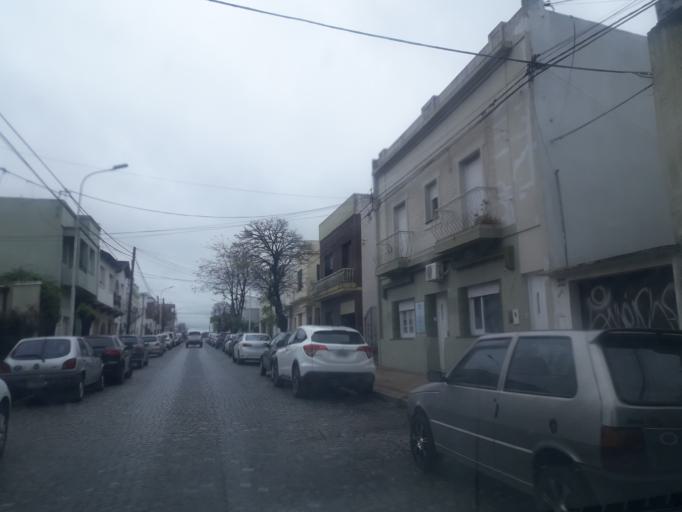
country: AR
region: Buenos Aires
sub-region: Partido de Tandil
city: Tandil
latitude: -37.3323
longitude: -59.1365
